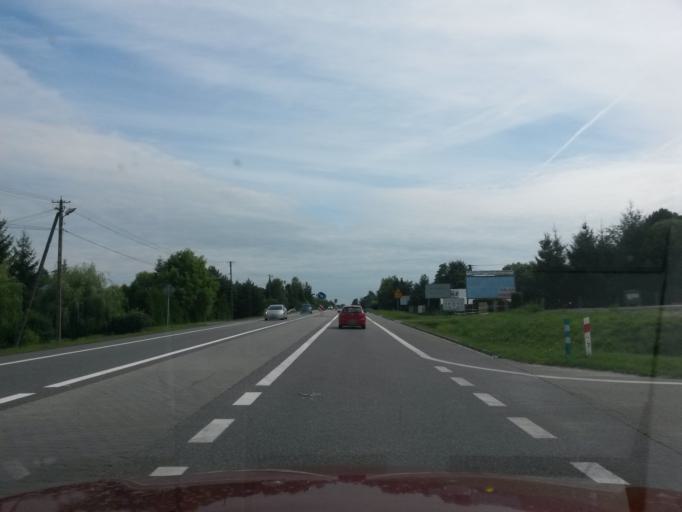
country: PL
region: Lesser Poland Voivodeship
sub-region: Powiat brzeski
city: Jasien
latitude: 49.9738
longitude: 20.5627
